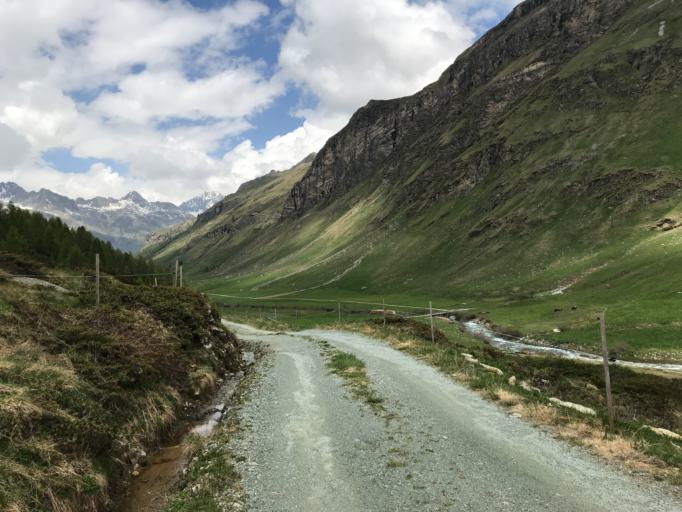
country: CH
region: Grisons
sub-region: Maloja District
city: Silvaplana
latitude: 46.3879
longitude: 9.7807
